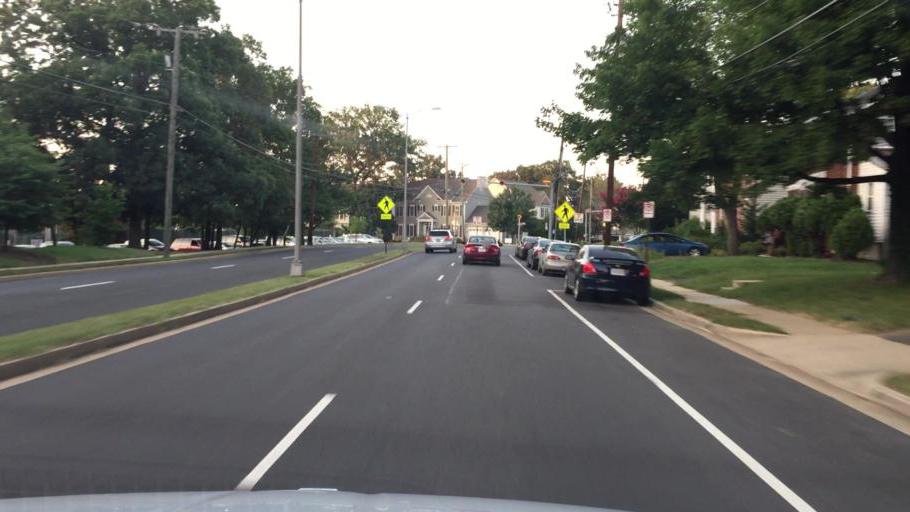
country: US
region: Virginia
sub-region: Fairfax County
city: Baileys Crossroads
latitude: 38.8707
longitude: -77.1252
